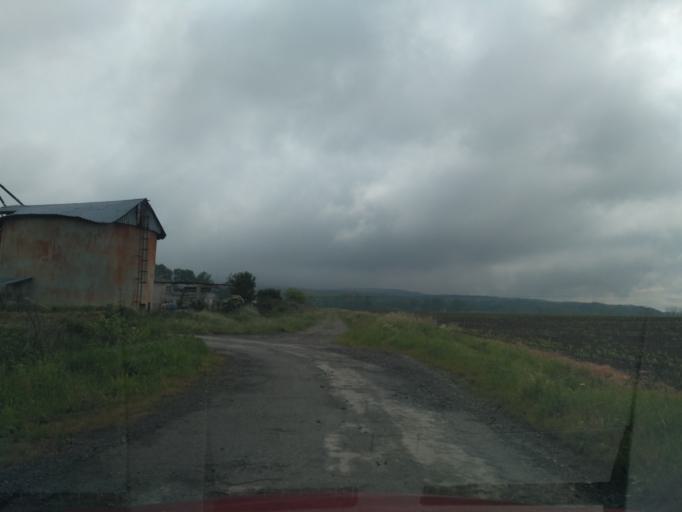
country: SK
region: Kosicky
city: Secovce
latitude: 48.7636
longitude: 21.4861
